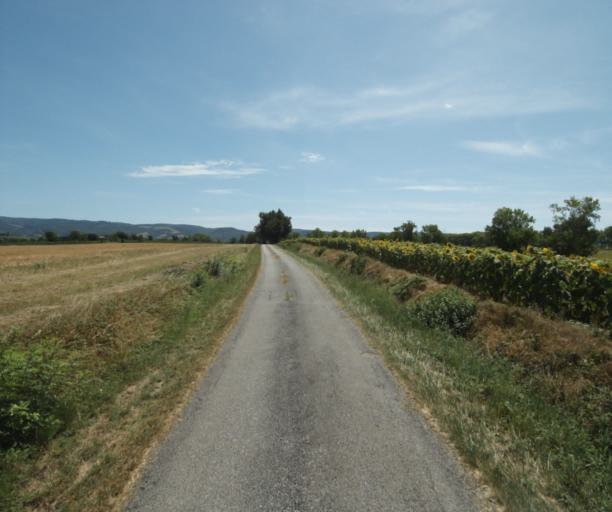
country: FR
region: Midi-Pyrenees
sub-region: Departement de la Haute-Garonne
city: Revel
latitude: 43.4923
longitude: 2.0353
